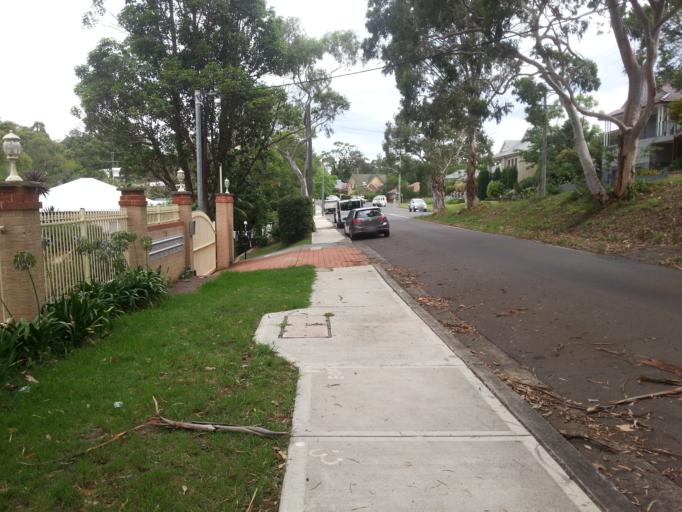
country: AU
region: New South Wales
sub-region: Wollongong
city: Mangerton
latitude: -34.4287
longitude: 150.8733
